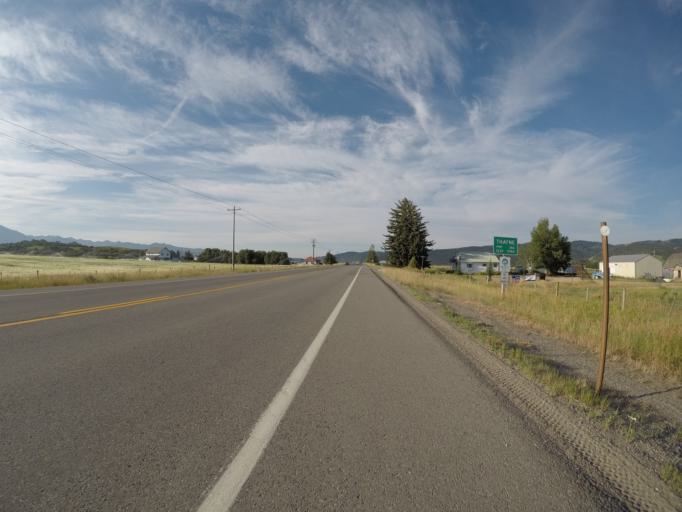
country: US
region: Wyoming
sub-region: Lincoln County
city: Afton
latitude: 42.9320
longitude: -111.0074
